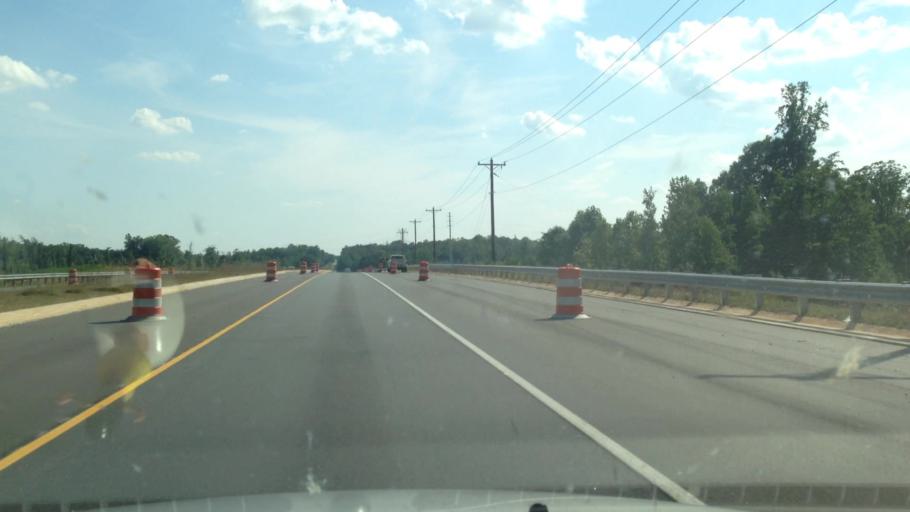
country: US
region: North Carolina
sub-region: Forsyth County
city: Walkertown
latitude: 36.1483
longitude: -80.1543
